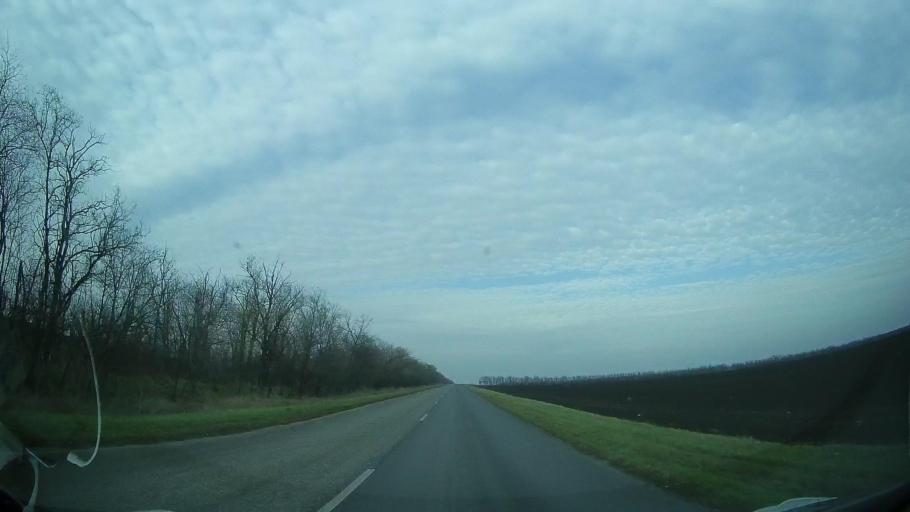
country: RU
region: Rostov
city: Zernograd
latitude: 46.9339
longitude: 40.3665
